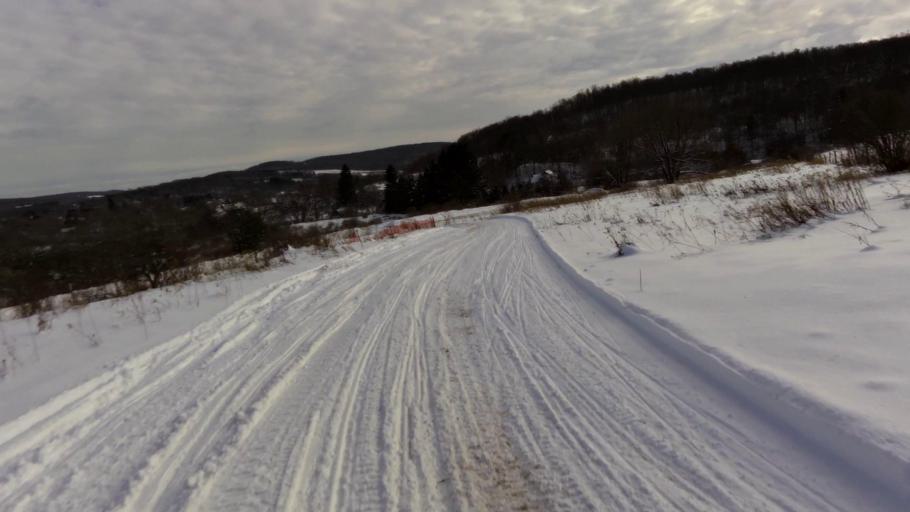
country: US
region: New York
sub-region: Cattaraugus County
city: Franklinville
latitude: 42.3397
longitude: -78.4743
